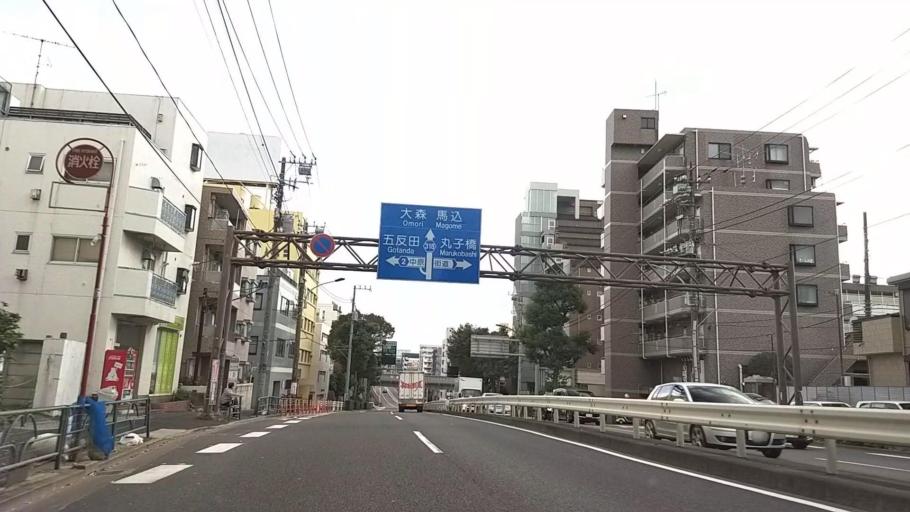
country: JP
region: Tokyo
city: Tokyo
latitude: 35.6065
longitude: 139.6957
